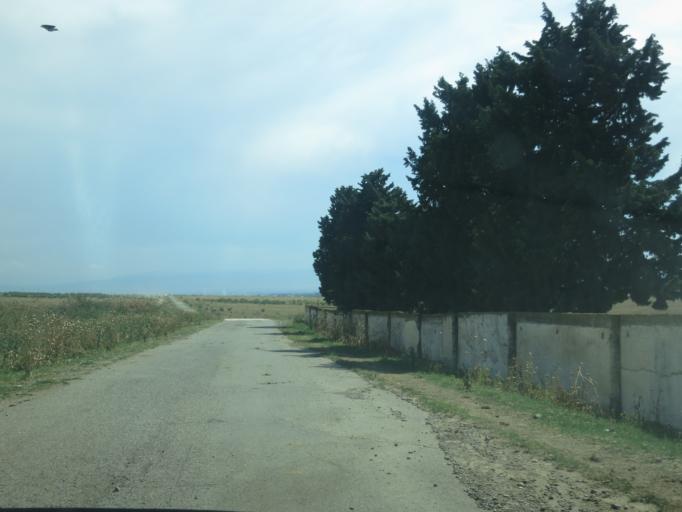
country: GE
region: Kvemo Kartli
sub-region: Gardabani
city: Gardabani
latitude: 41.4977
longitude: 45.1894
